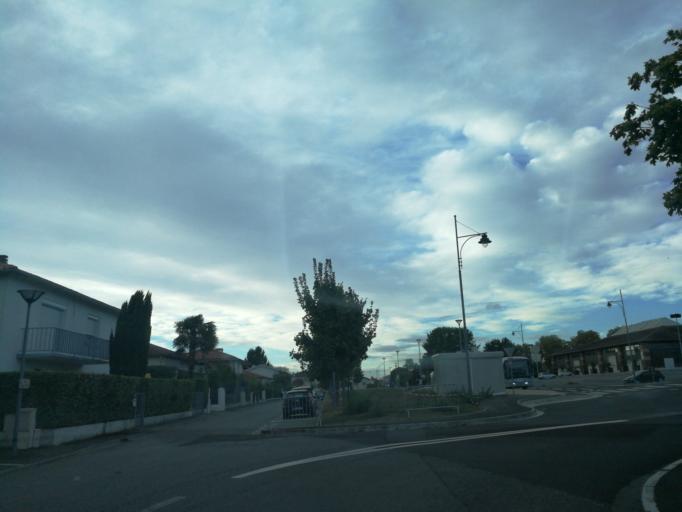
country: FR
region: Midi-Pyrenees
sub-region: Departement de la Haute-Garonne
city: L'Union
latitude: 43.6545
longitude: 1.4828
